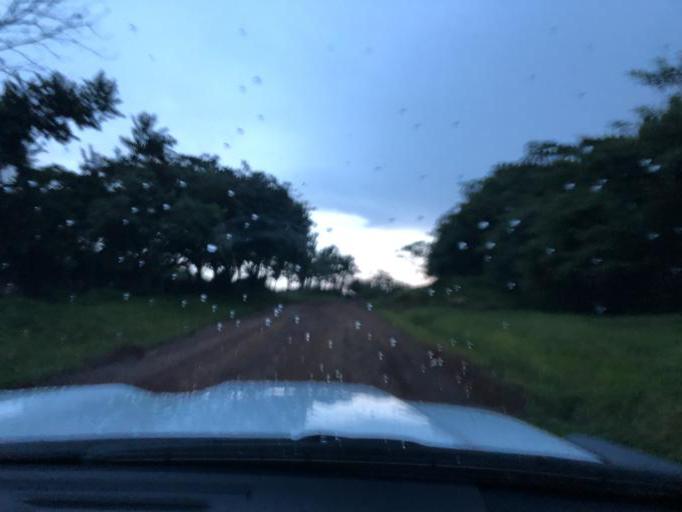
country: NI
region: Chontales
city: La Libertad
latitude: 12.1566
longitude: -85.1791
